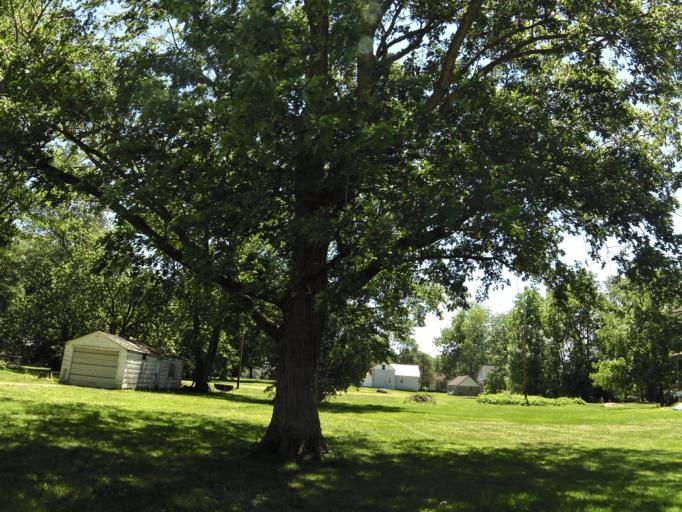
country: US
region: Illinois
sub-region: Livingston County
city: Chatsworth
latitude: 40.7563
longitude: -88.1843
